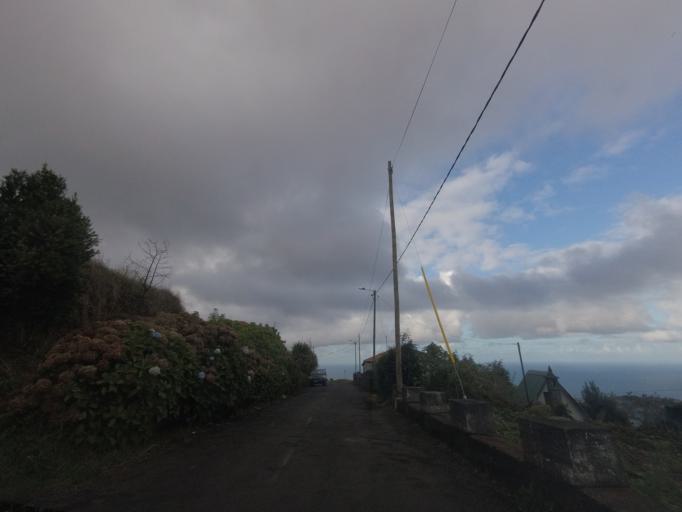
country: PT
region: Madeira
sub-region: Santana
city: Santana
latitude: 32.8014
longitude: -16.8891
